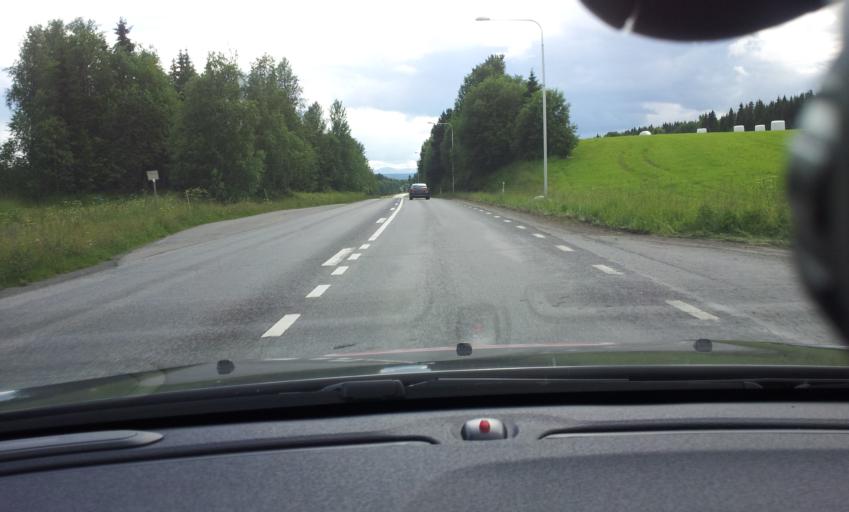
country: SE
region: Jaemtland
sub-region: Are Kommun
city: Jarpen
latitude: 63.3339
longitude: 13.4164
